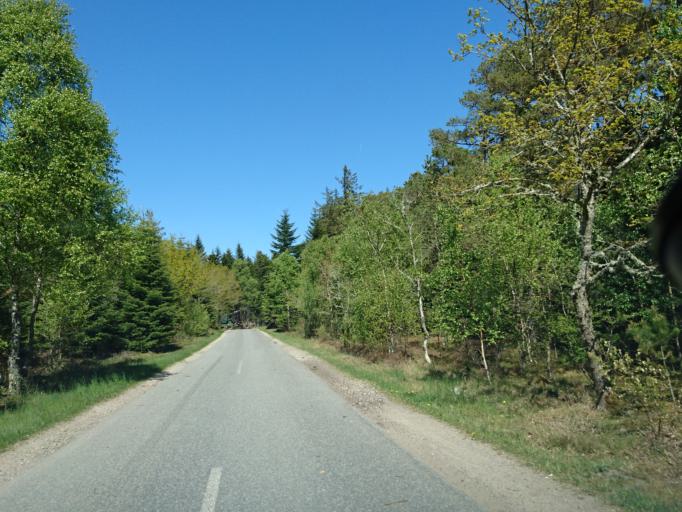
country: DK
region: North Denmark
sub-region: Hjorring Kommune
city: Sindal
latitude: 57.5954
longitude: 10.2291
